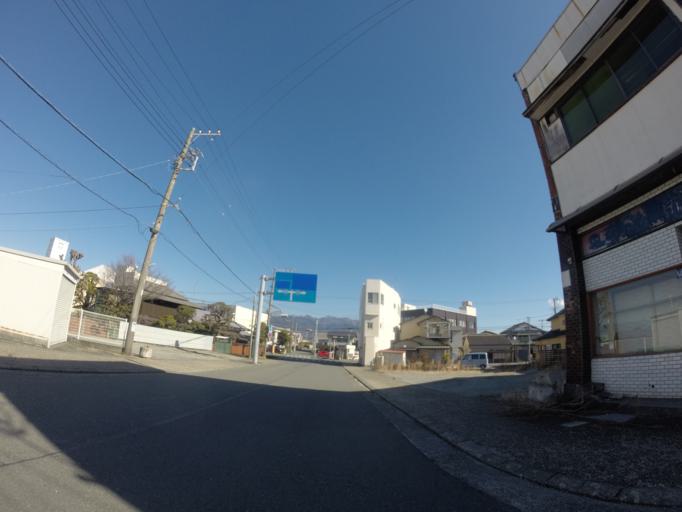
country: JP
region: Shizuoka
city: Fuji
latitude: 35.1443
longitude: 138.7038
